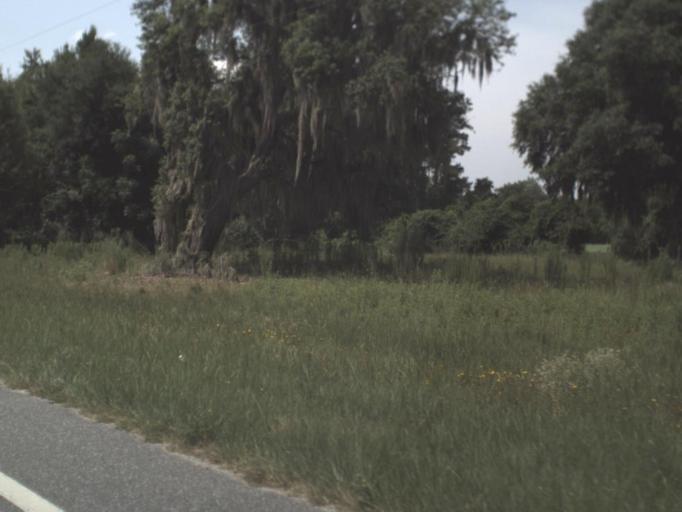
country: US
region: Georgia
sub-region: Echols County
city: Statenville
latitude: 30.5870
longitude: -83.0922
